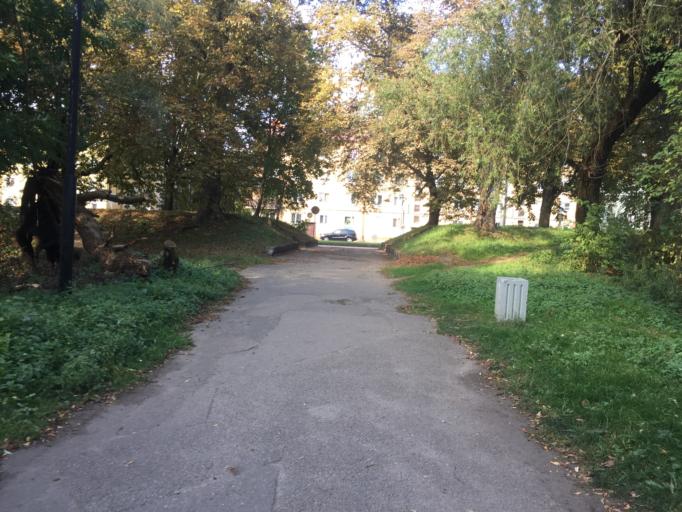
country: RU
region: Kaliningrad
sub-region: Gorod Kaliningrad
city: Kaliningrad
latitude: 54.6944
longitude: 20.5070
